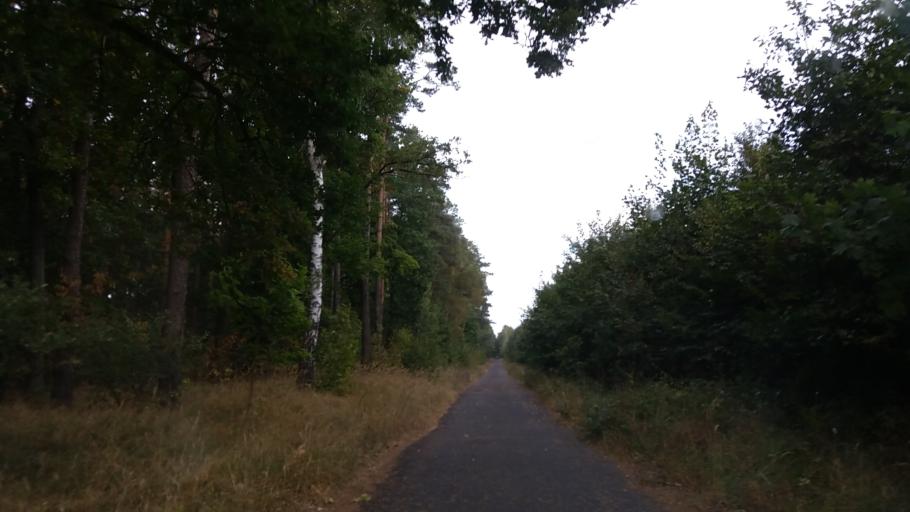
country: PL
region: Lubusz
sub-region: Powiat strzelecko-drezdenecki
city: Strzelce Krajenskie
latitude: 52.9619
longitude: 15.4550
